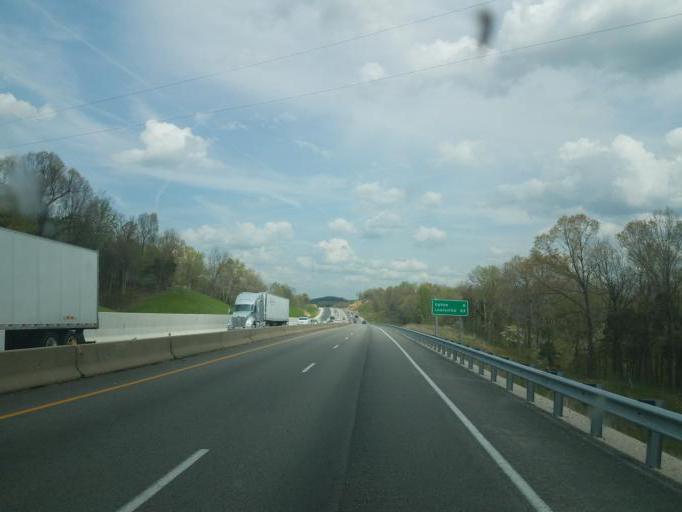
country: US
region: Kentucky
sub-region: Hart County
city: Munfordville
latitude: 37.3959
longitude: -85.8827
